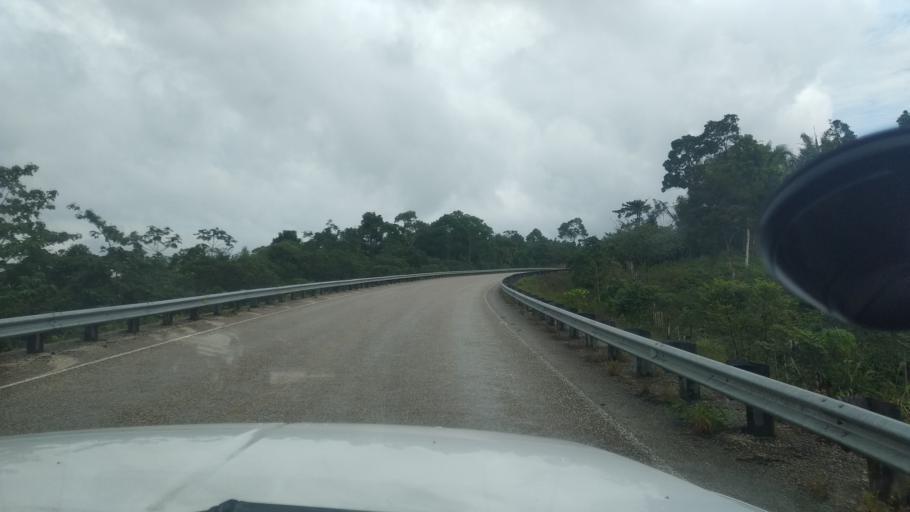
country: GT
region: Peten
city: San Luis
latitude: 16.1958
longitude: -89.1666
